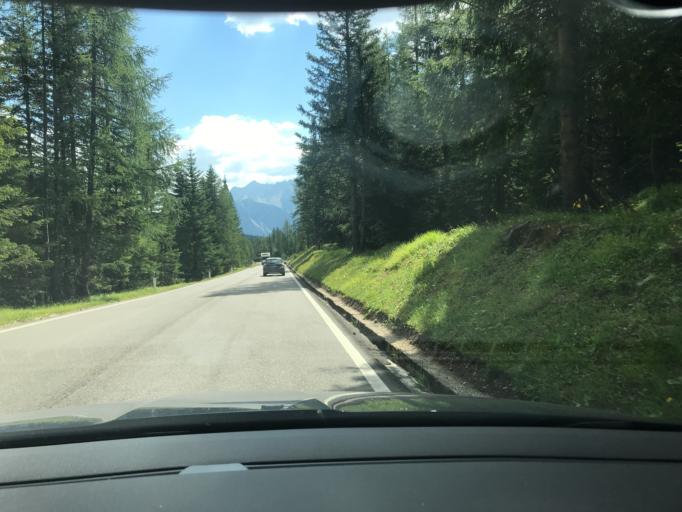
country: IT
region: Veneto
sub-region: Provincia di Belluno
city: Selva di Cadore
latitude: 46.5221
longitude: 12.0447
